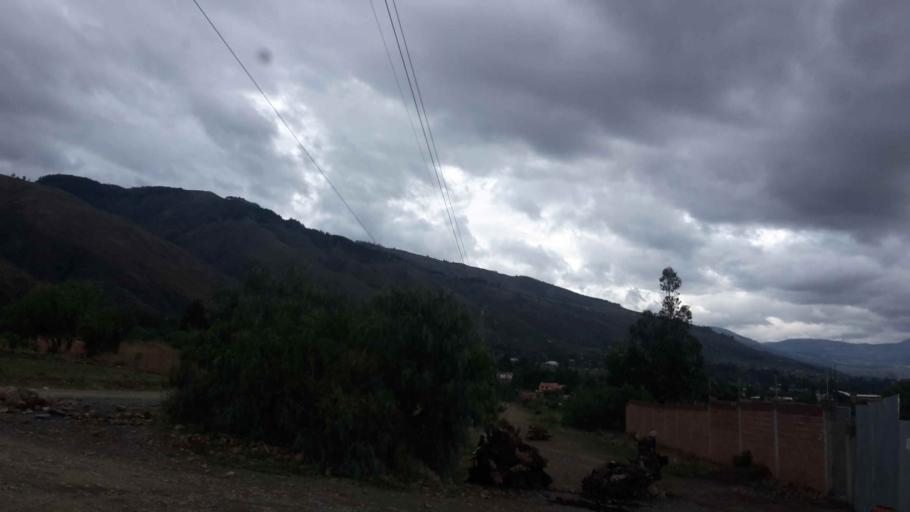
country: BO
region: Cochabamba
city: Cochabamba
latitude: -17.3779
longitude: -66.0596
